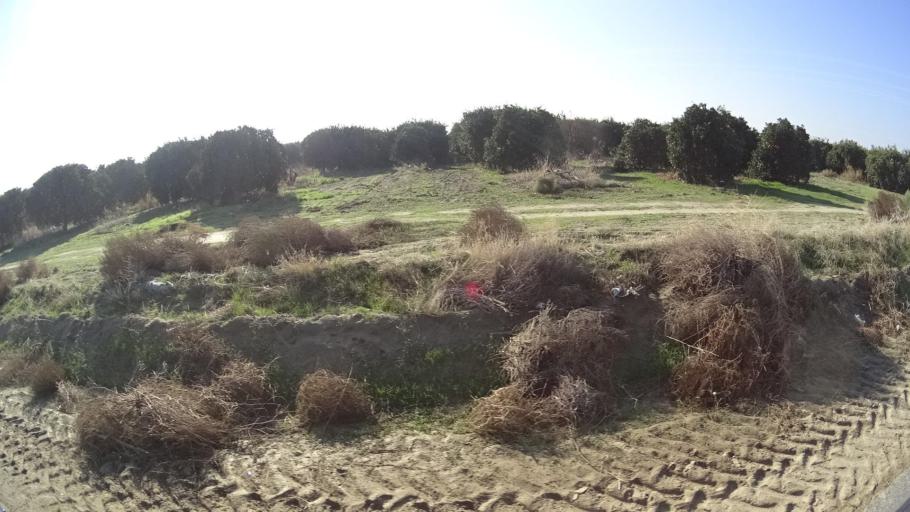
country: US
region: California
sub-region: Kern County
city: Weedpatch
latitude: 35.1220
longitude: -118.9370
